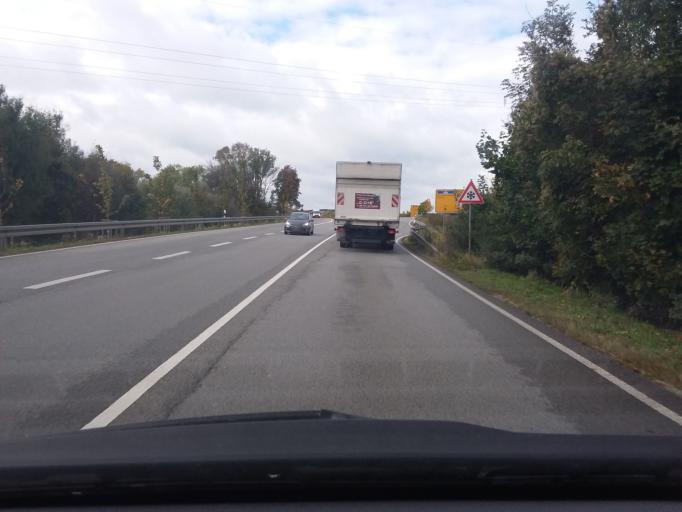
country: DE
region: Bavaria
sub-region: Upper Bavaria
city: Bergkirchen
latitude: 48.2378
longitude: 11.3579
